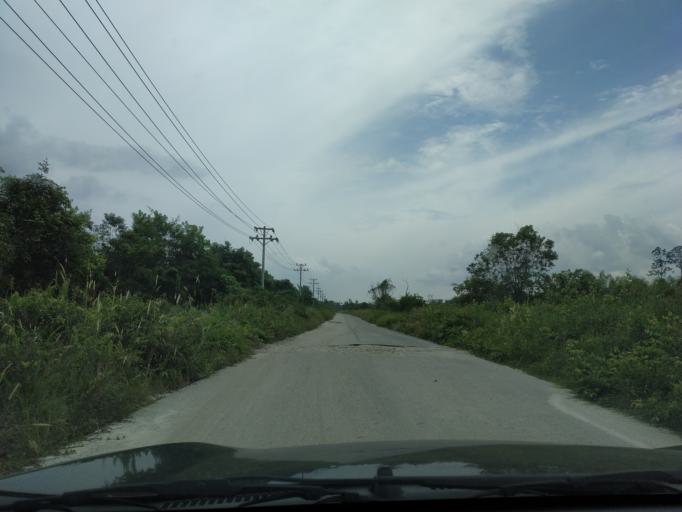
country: ID
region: Riau
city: Siak Sri Indrapura
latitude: 0.9113
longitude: 102.3049
